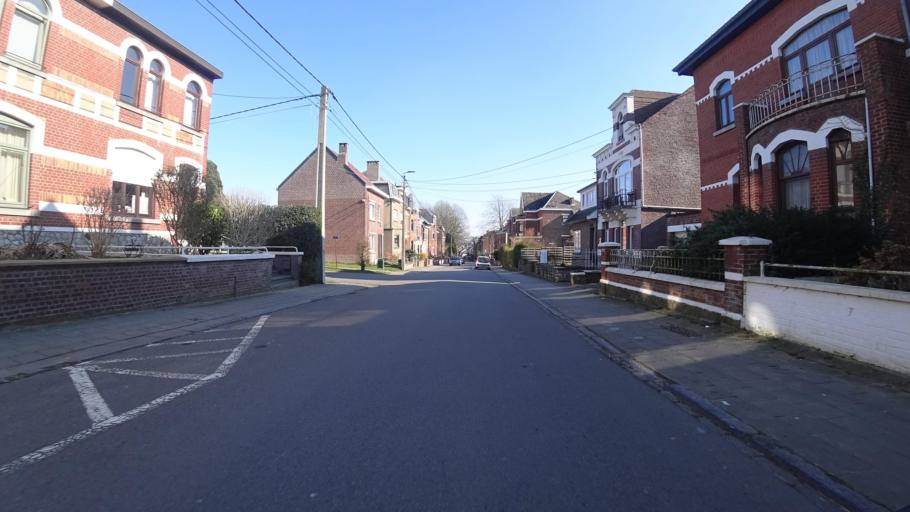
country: BE
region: Wallonia
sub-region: Province de Namur
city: Gembloux
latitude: 50.5619
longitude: 4.6854
